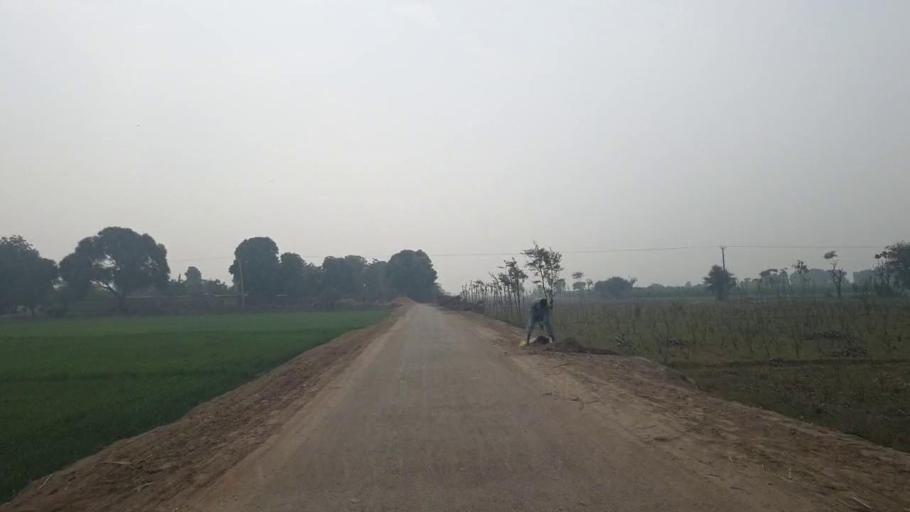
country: PK
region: Sindh
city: Tando Adam
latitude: 25.7054
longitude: 68.6263
